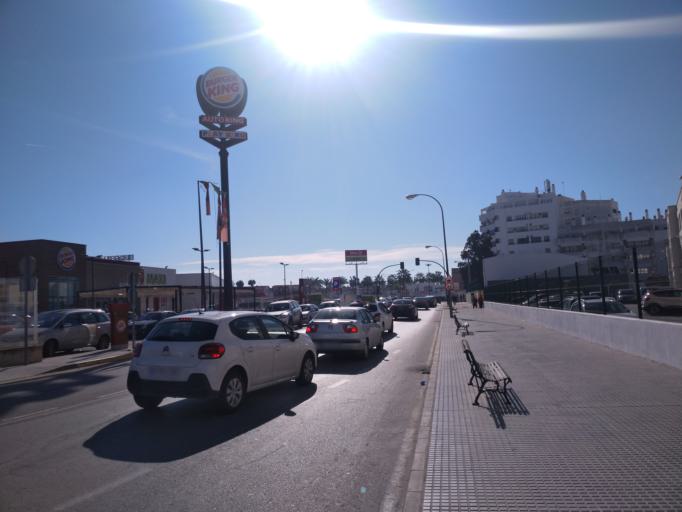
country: ES
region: Andalusia
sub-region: Provincia de Cadiz
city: San Fernando
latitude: 36.4699
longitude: -6.1903
